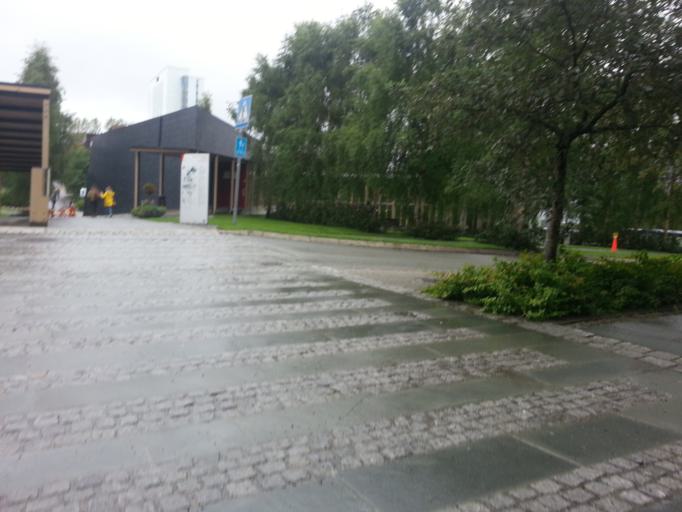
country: NO
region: Troms
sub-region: Tromso
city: Tromso
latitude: 69.6810
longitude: 18.9743
